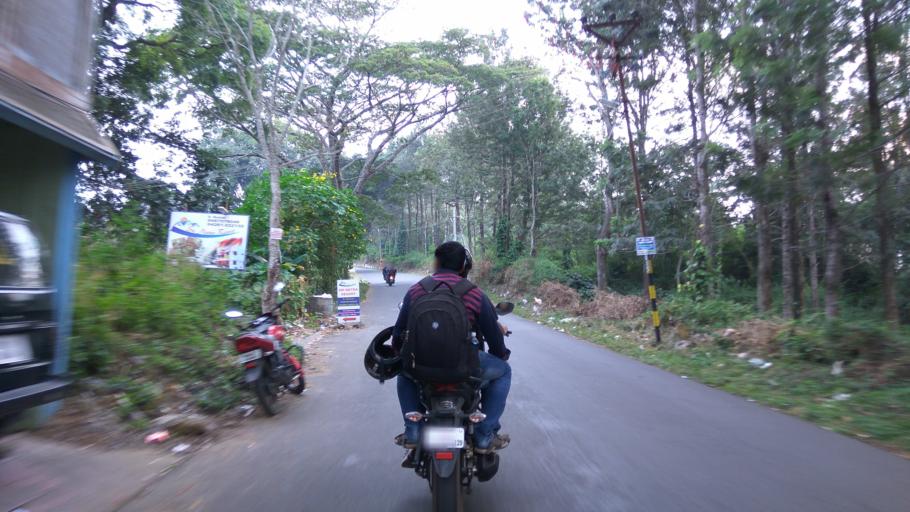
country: IN
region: Tamil Nadu
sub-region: Salem
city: Salem
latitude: 11.7813
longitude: 78.2111
